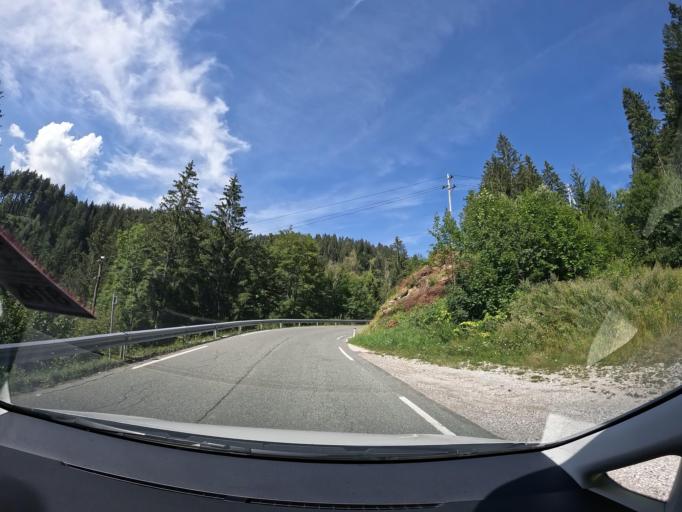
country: AT
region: Carinthia
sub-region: Politischer Bezirk Villach Land
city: Sankt Jakob
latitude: 46.5540
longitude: 14.0791
